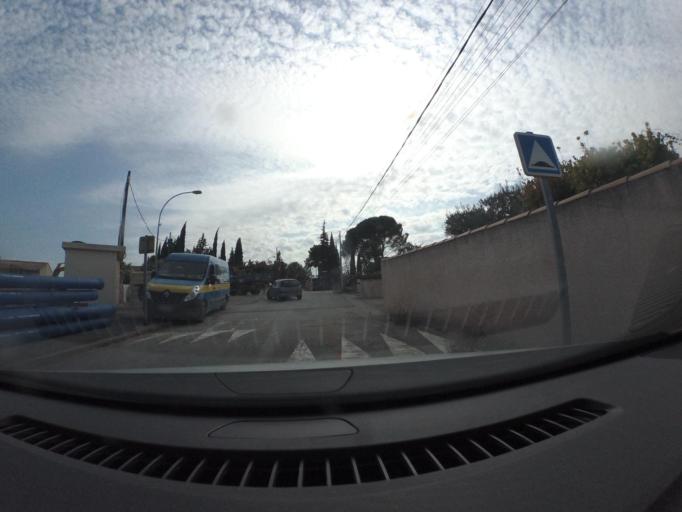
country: FR
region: Languedoc-Roussillon
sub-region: Departement de l'Herault
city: Baillargues
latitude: 43.6665
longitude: 4.0129
